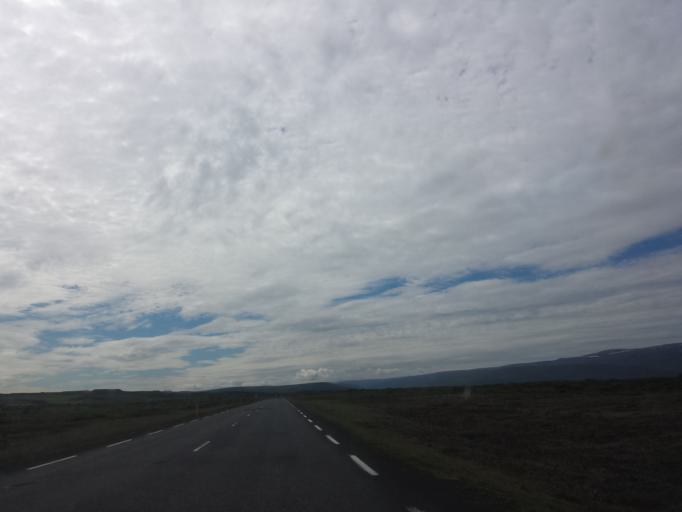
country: IS
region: Northeast
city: Husavik
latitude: 65.9579
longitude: -17.4270
